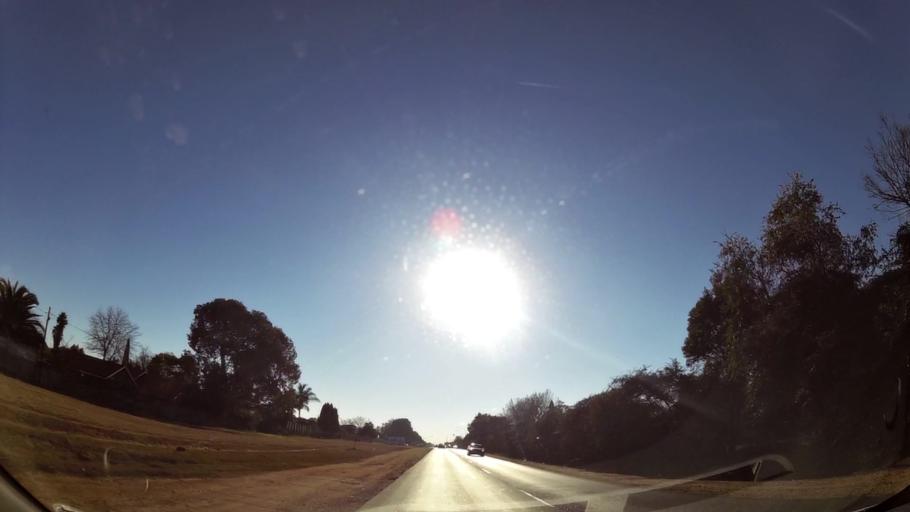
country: ZA
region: Gauteng
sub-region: Ekurhuleni Metropolitan Municipality
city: Tembisa
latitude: -26.0573
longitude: 28.2302
